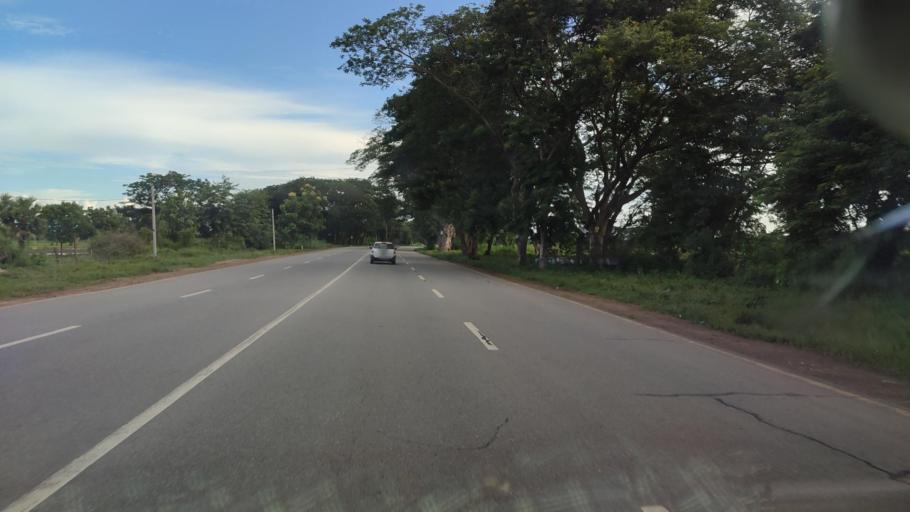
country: MM
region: Mandalay
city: Yamethin
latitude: 20.2307
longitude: 96.1794
